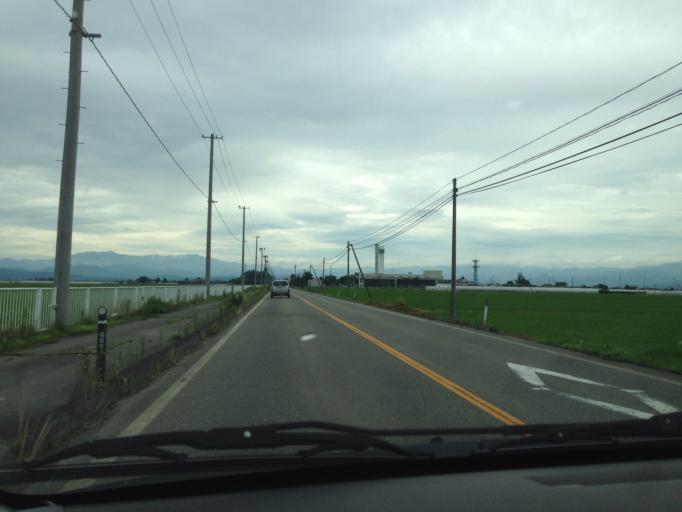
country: JP
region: Fukushima
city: Kitakata
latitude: 37.4865
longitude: 139.8742
